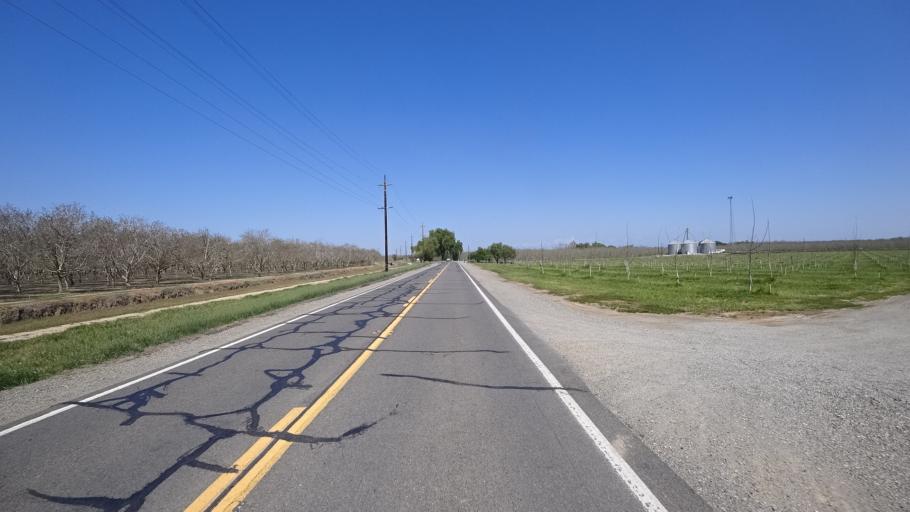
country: US
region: California
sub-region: Glenn County
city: Willows
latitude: 39.5268
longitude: -122.0127
